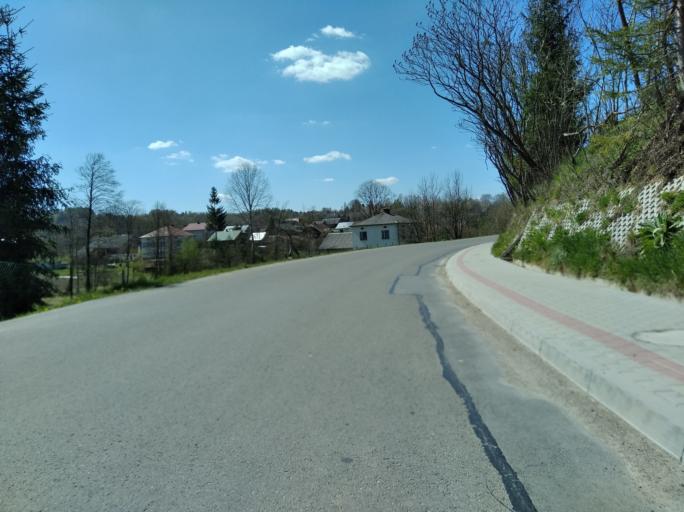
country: PL
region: Subcarpathian Voivodeship
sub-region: Powiat brzozowski
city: Golcowa
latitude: 49.7701
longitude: 22.0299
